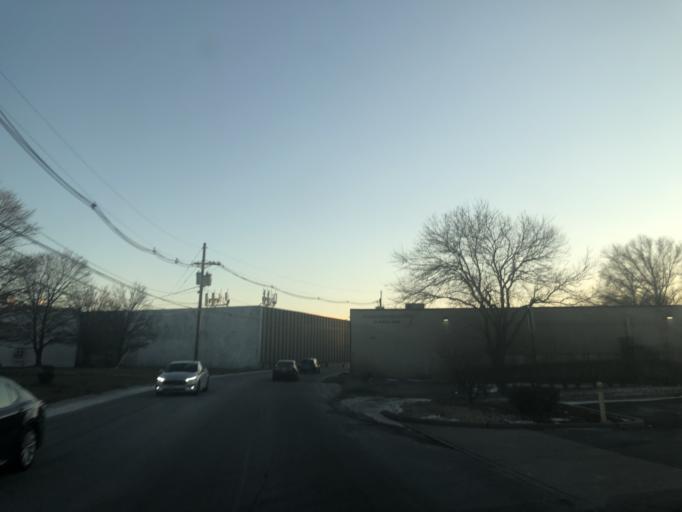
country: US
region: New Jersey
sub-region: Hudson County
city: Jersey City
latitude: 40.7031
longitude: -74.0645
